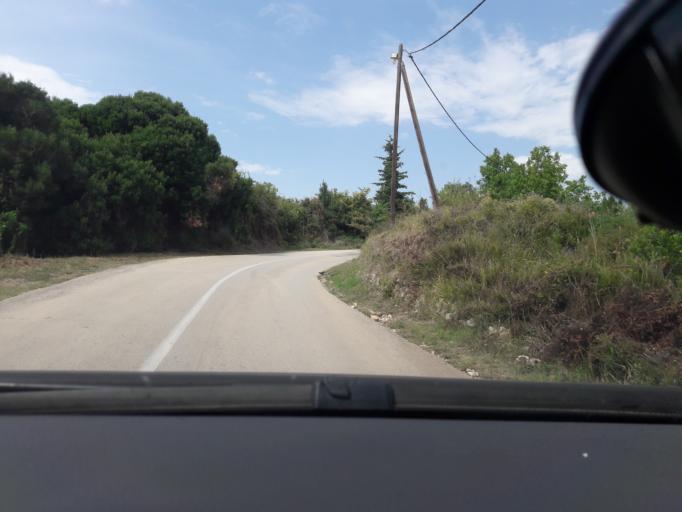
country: HR
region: Zadarska
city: Nin
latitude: 44.1675
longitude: 15.1884
